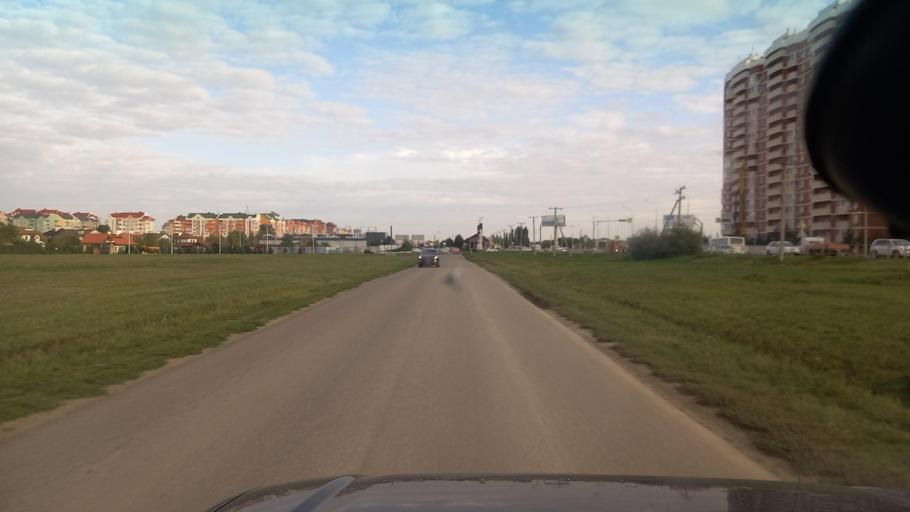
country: RU
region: Krasnodarskiy
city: Krasnodar
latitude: 45.1151
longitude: 38.9204
